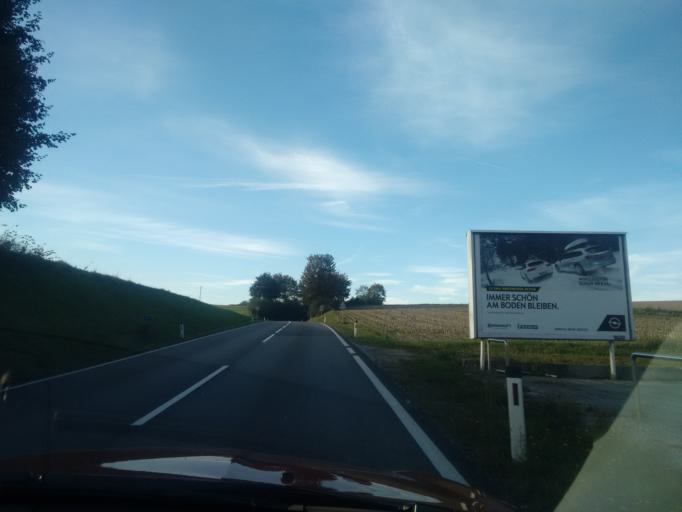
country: AT
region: Upper Austria
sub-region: Politischer Bezirk Vocklabruck
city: Niederthalheim
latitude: 48.1489
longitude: 13.7334
